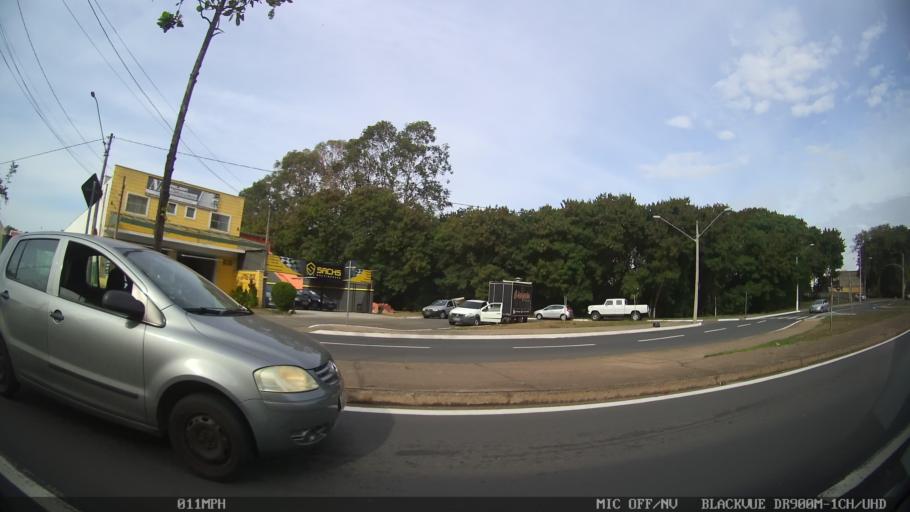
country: BR
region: Sao Paulo
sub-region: Piracicaba
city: Piracicaba
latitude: -22.7435
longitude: -47.6306
